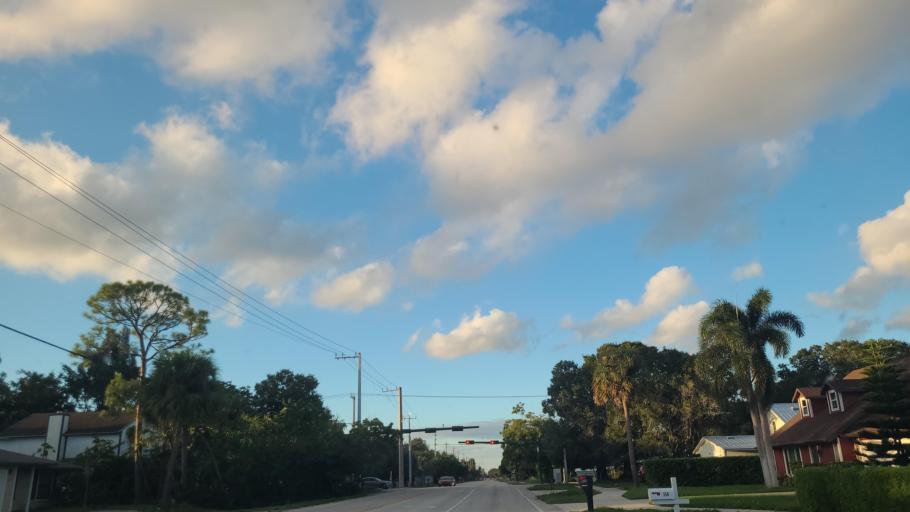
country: US
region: Florida
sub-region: Indian River County
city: Vero Beach South
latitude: 27.6081
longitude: -80.4058
